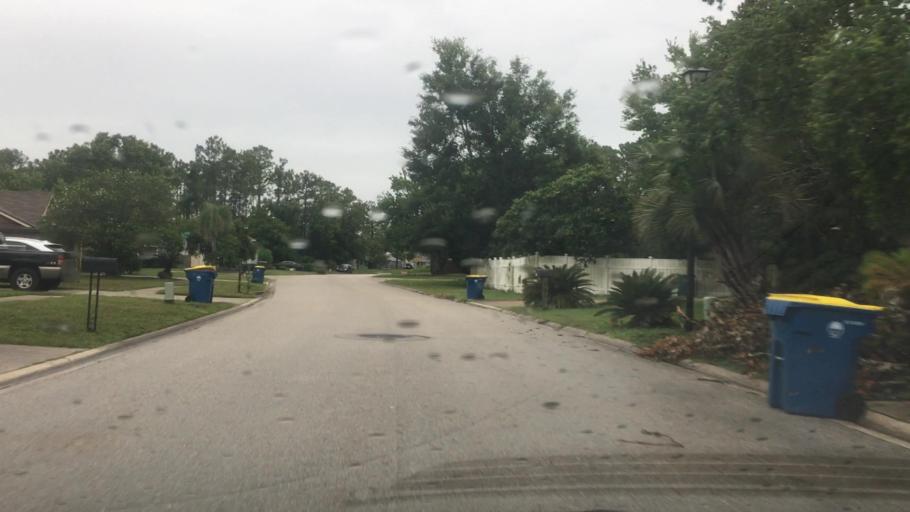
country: US
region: Florida
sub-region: Duval County
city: Atlantic Beach
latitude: 30.3236
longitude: -81.4660
